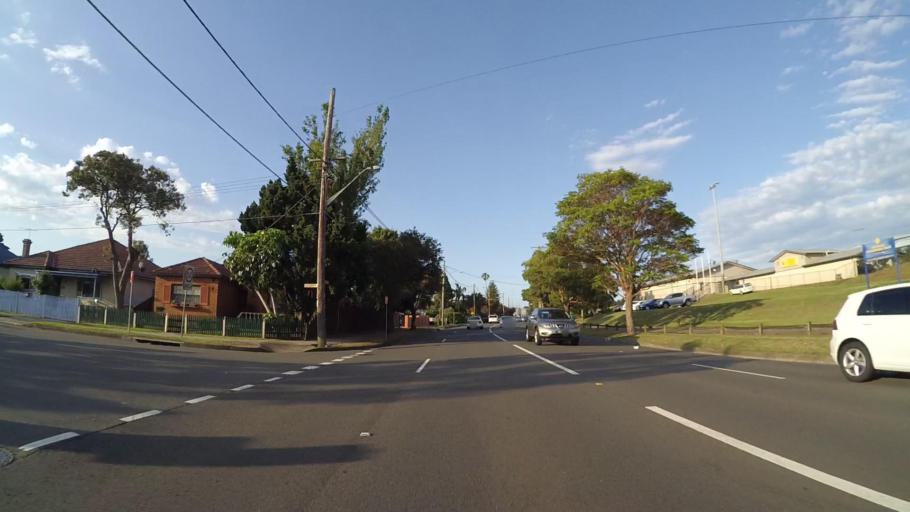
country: AU
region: New South Wales
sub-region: Rockdale
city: Brighton-Le-Sands
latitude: -33.9639
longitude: 151.1431
